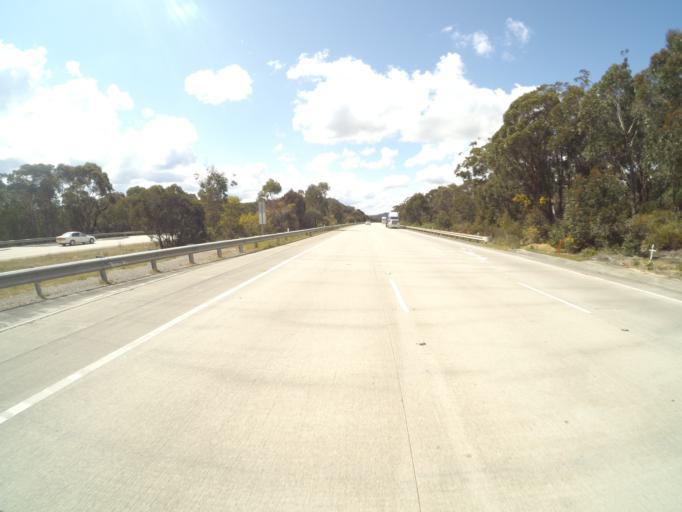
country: AU
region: New South Wales
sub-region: Wingecarribee
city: Mittagong
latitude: -34.4339
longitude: 150.4311
